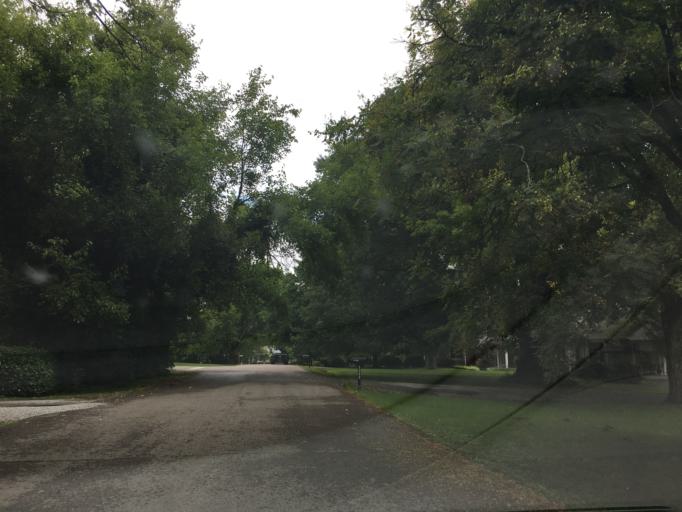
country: US
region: Tennessee
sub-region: Davidson County
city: Oak Hill
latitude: 36.1075
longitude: -86.7797
